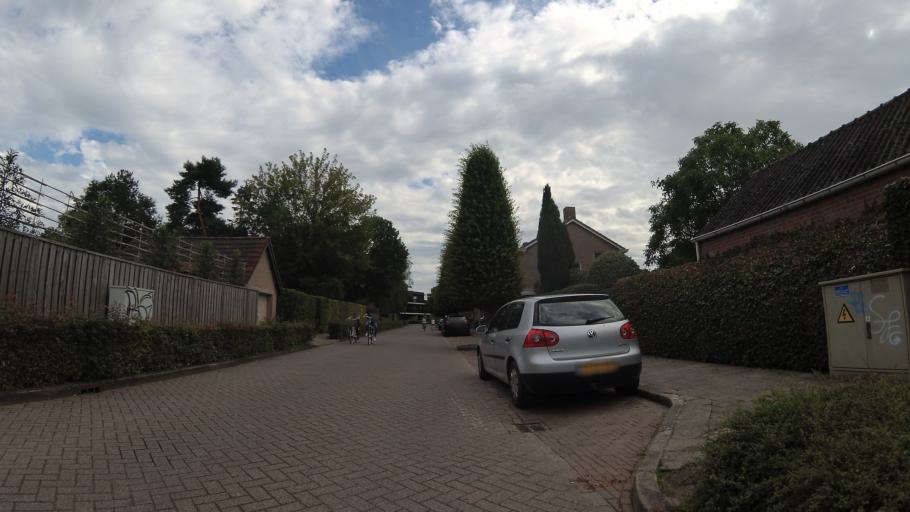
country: NL
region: North Brabant
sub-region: Gemeente Made en Drimmelen
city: Made
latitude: 51.6748
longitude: 4.7892
